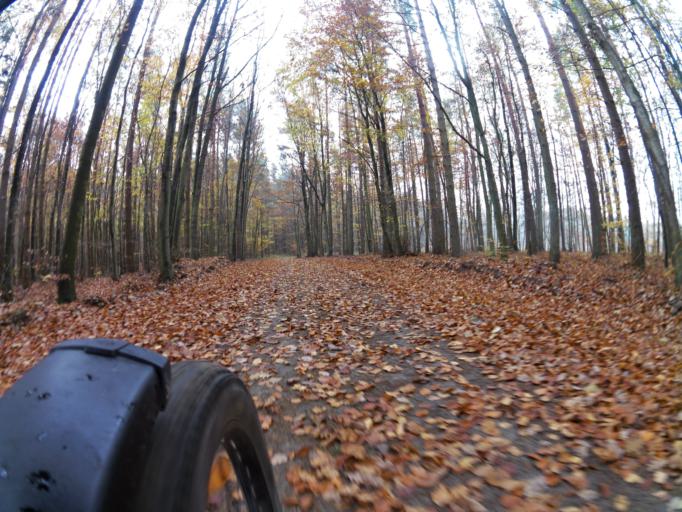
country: PL
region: Pomeranian Voivodeship
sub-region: Powiat pucki
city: Krokowa
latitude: 54.7726
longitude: 18.0925
